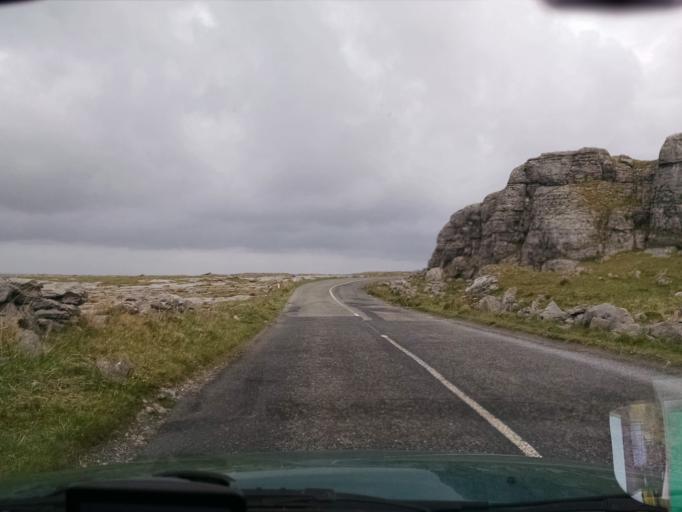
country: IE
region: Connaught
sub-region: County Galway
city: Bearna
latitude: 53.0671
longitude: -9.3593
